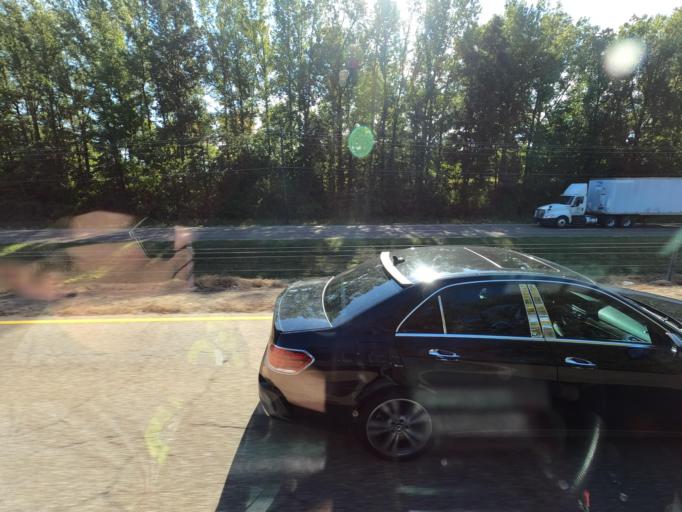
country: US
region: Tennessee
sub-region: Tipton County
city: Brighton
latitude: 35.5000
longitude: -89.7200
